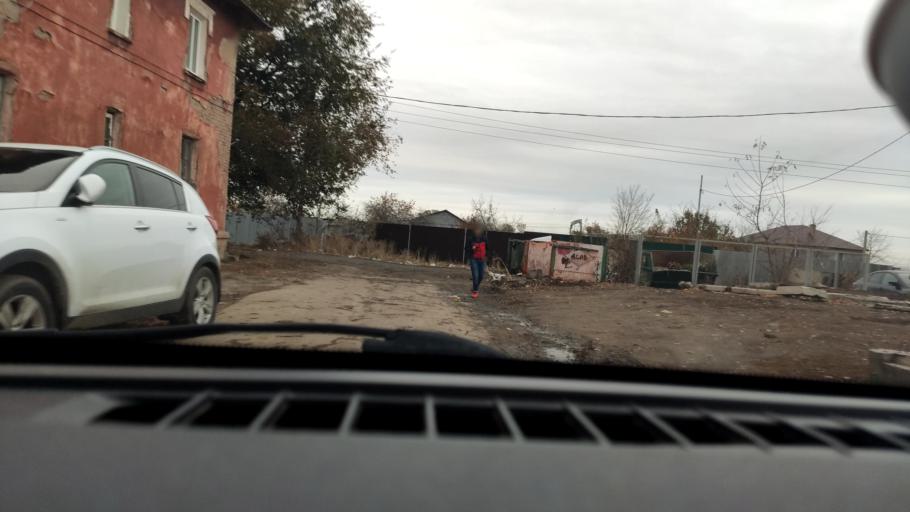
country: RU
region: Samara
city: Samara
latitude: 53.1837
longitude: 50.2100
